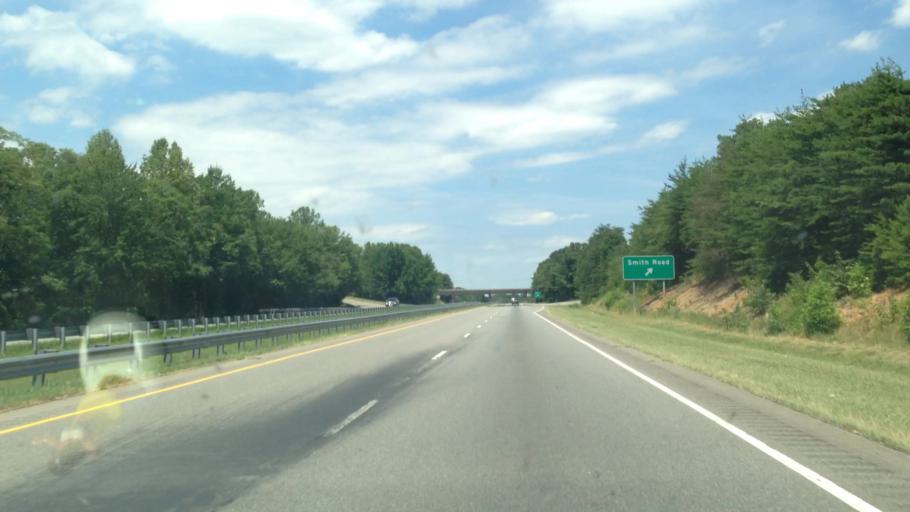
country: US
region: North Carolina
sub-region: Rockingham County
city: Stoneville
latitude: 36.4980
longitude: -79.9224
